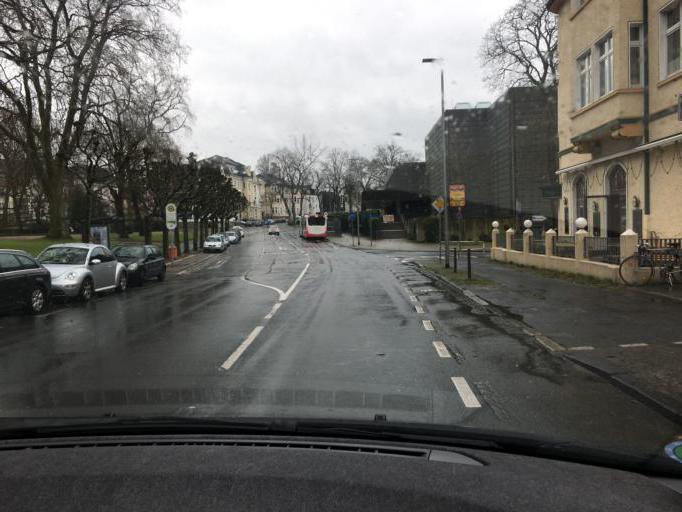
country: DE
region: North Rhine-Westphalia
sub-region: Regierungsbezirk Arnsberg
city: Bochum
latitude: 51.4885
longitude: 7.2213
